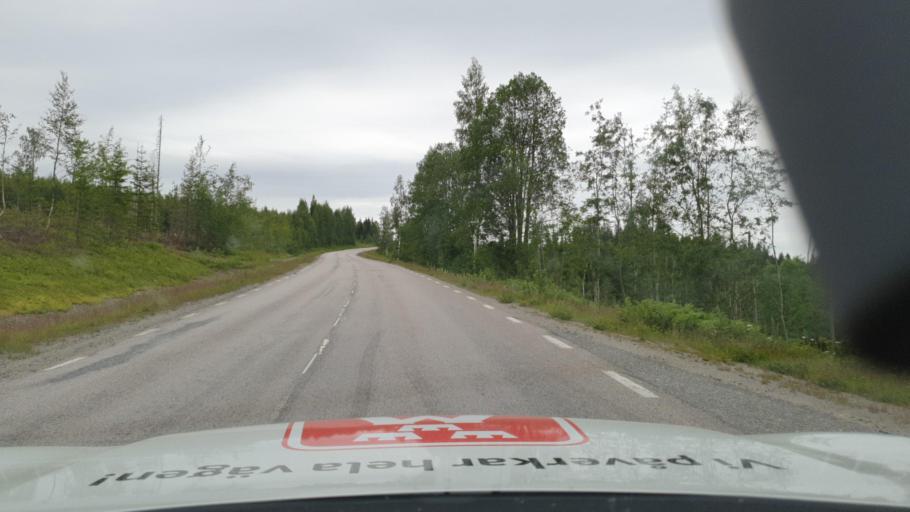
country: SE
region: Vaesterbotten
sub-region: Vannas Kommun
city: Vaennaes
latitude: 63.7902
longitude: 19.8224
